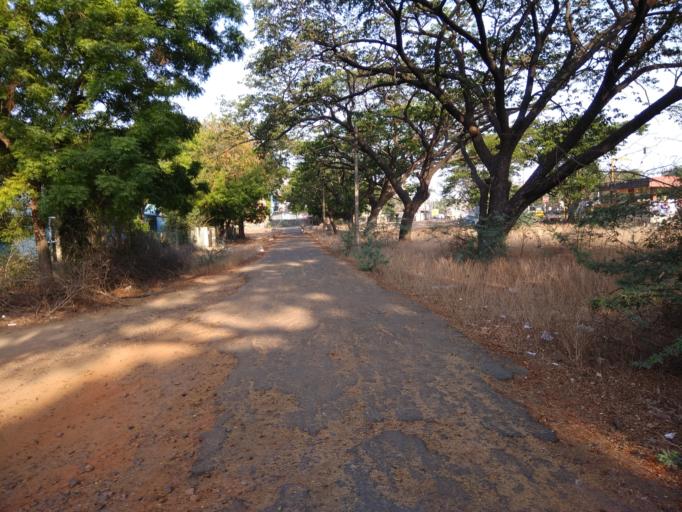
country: IN
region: Tamil Nadu
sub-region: Kancheepuram
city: Saint Thomas Mount
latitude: 13.0174
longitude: 80.1891
